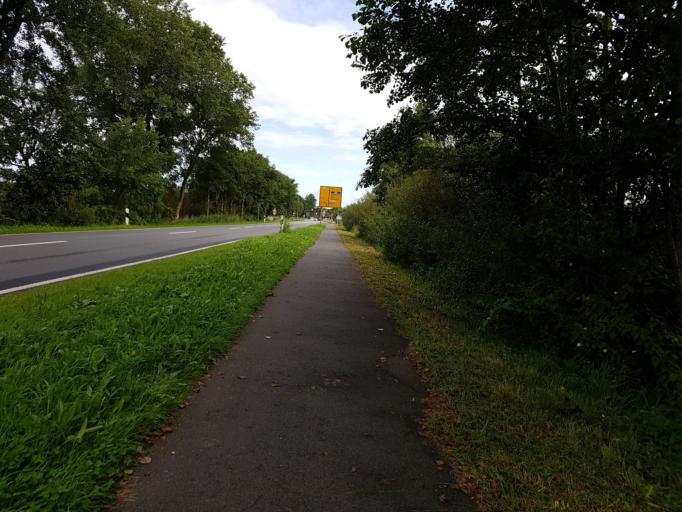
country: DE
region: Lower Saxony
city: Wittmund
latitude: 53.5651
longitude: 7.7840
